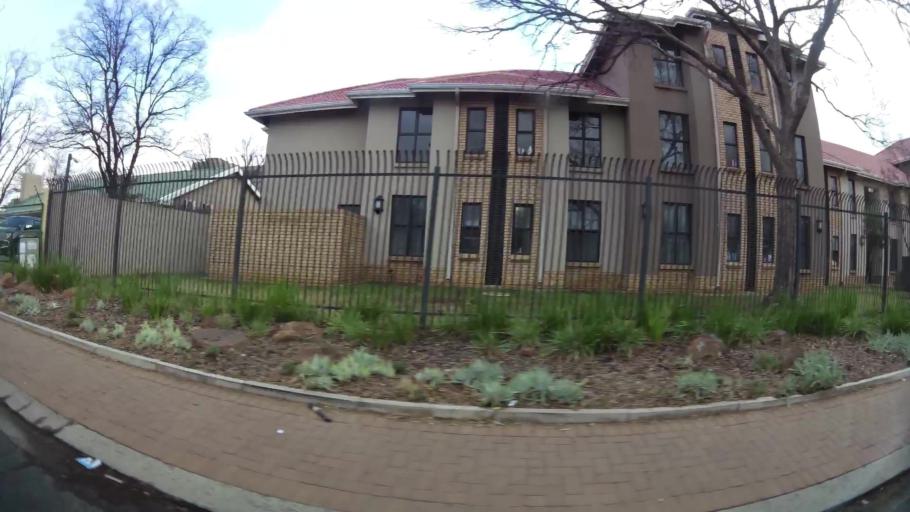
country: ZA
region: Orange Free State
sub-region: Mangaung Metropolitan Municipality
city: Bloemfontein
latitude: -29.1187
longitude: 26.1860
